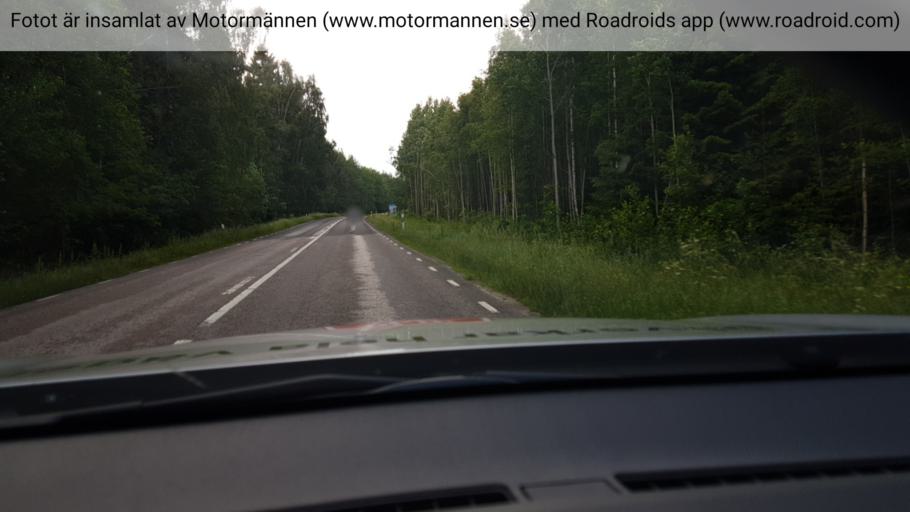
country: SE
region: Vaestra Goetaland
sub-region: Hjo Kommun
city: Hjo
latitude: 58.1813
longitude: 14.2034
